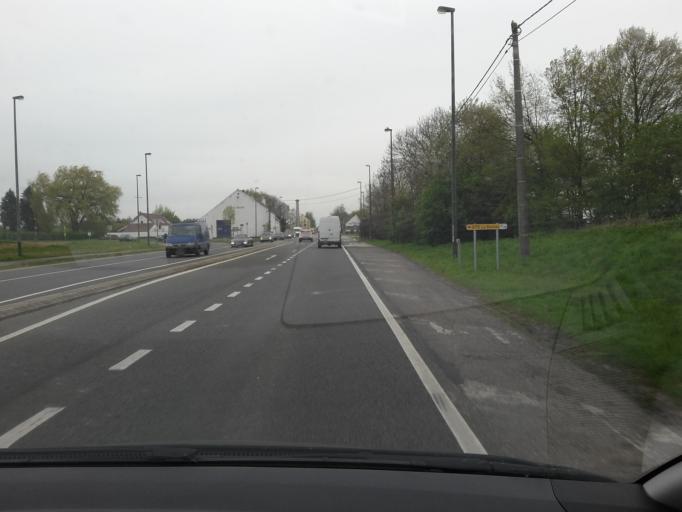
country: BE
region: Wallonia
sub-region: Province du Brabant Wallon
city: Waterloo
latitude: 50.6698
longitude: 4.4131
